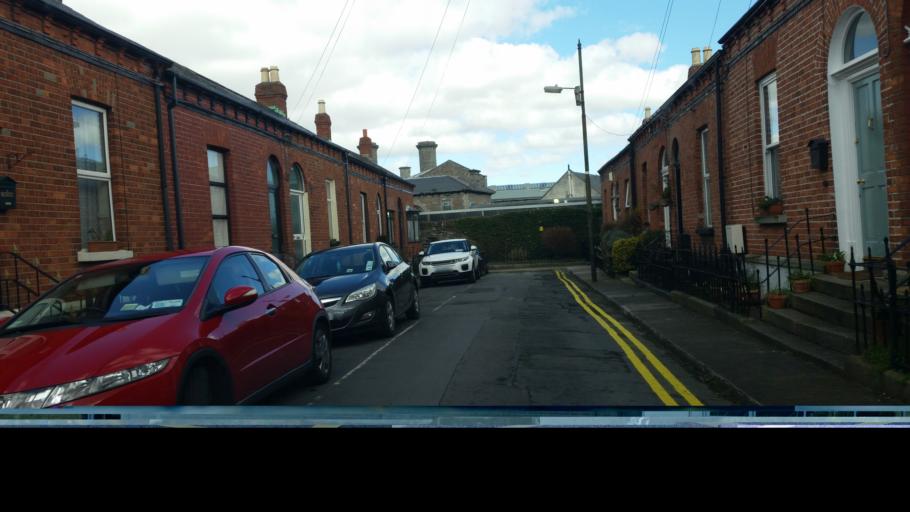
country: IE
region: Leinster
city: Drumcondra
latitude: 53.3611
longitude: -6.2700
